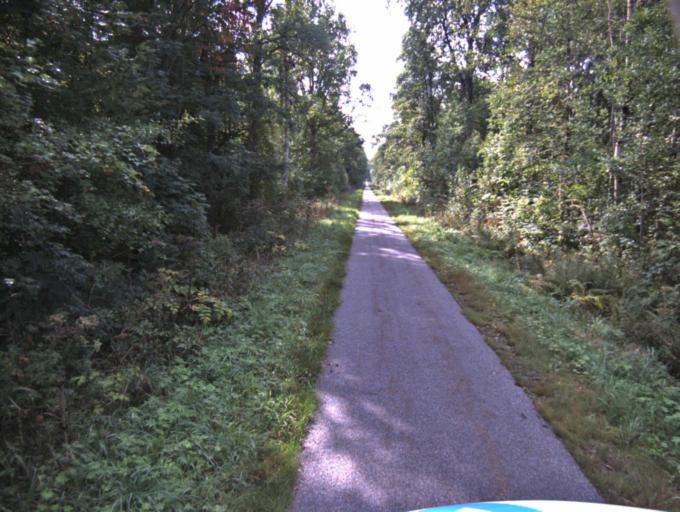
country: SE
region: Vaestra Goetaland
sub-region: Tranemo Kommun
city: Limmared
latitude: 57.6537
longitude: 13.3616
